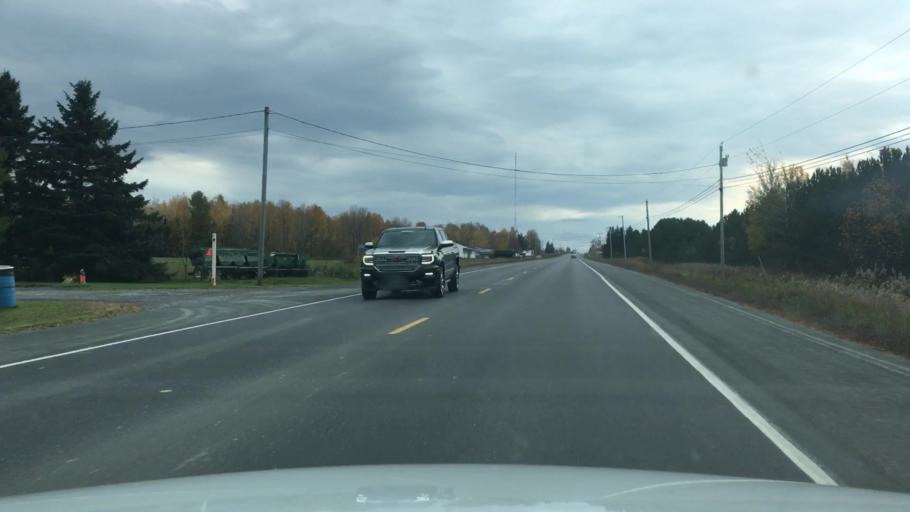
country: US
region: Maine
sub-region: Aroostook County
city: Caribou
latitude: 46.7739
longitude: -67.9895
